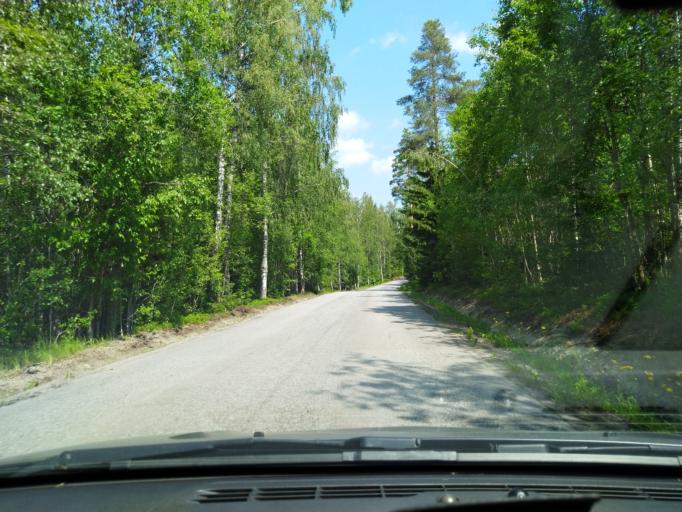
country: FI
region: Uusimaa
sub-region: Helsinki
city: Saukkola
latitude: 60.3617
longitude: 24.0976
